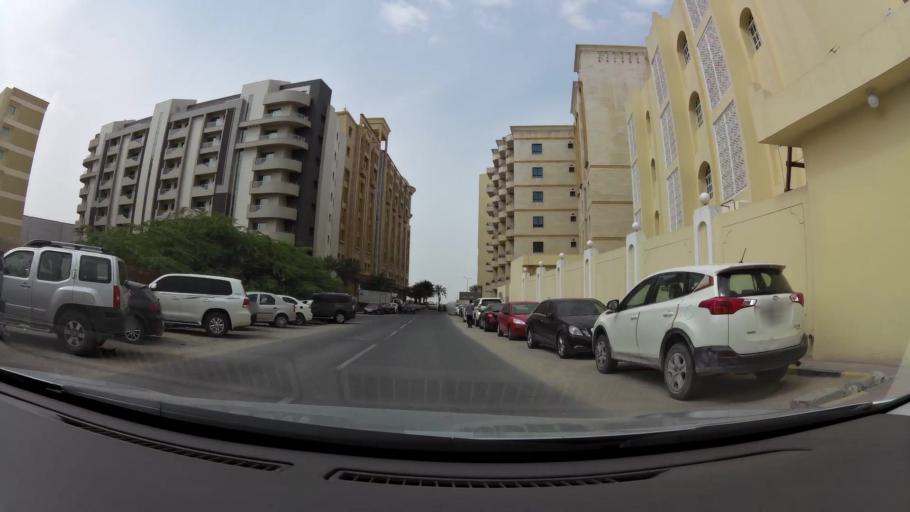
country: QA
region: Baladiyat ad Dawhah
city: Doha
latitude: 25.2840
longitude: 51.4967
